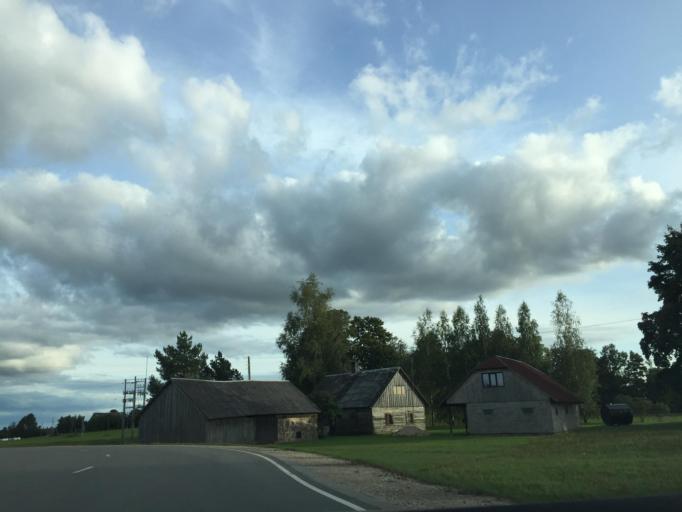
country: LV
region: Nereta
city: Nereta
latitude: 56.2525
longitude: 25.2160
